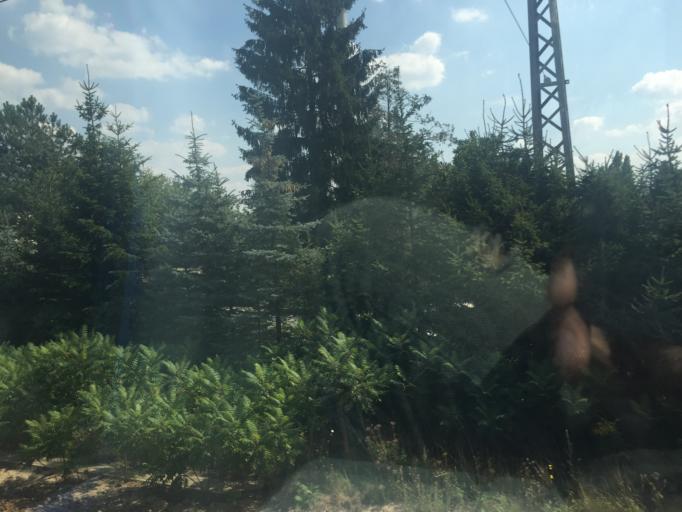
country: DE
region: Brandenburg
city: Ortrand
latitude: 51.3700
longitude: 13.7618
